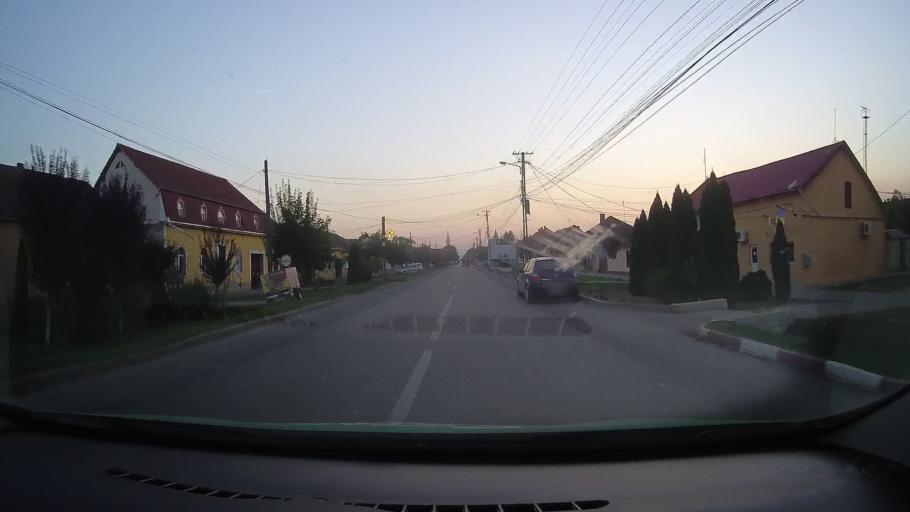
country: RO
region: Arad
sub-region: Comuna Santana
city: Santana
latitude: 46.3463
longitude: 21.5036
